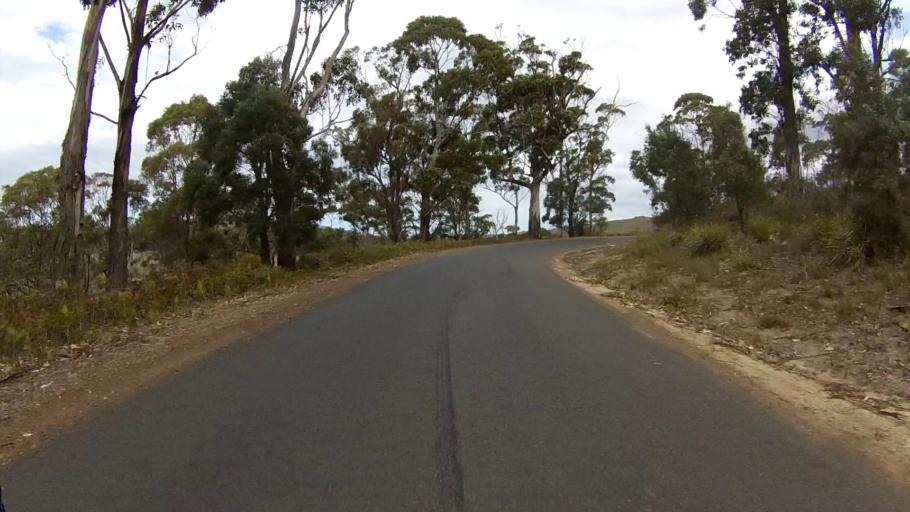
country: AU
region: Tasmania
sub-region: Sorell
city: Sorell
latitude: -42.6003
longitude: 147.9261
